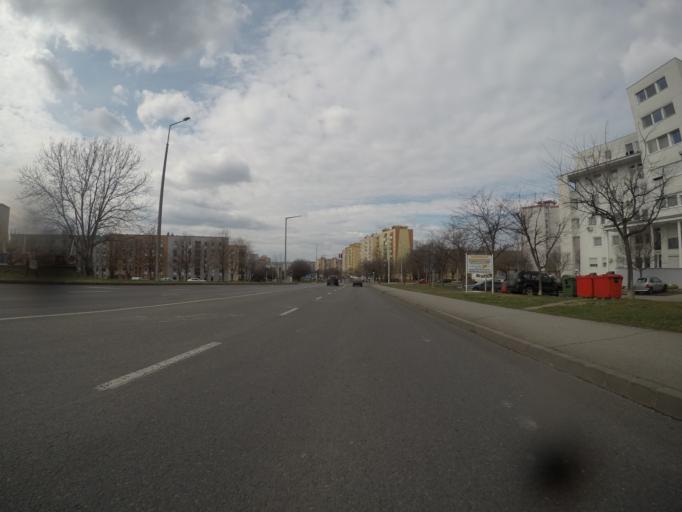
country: HU
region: Baranya
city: Pecs
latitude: 46.0371
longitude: 18.2281
